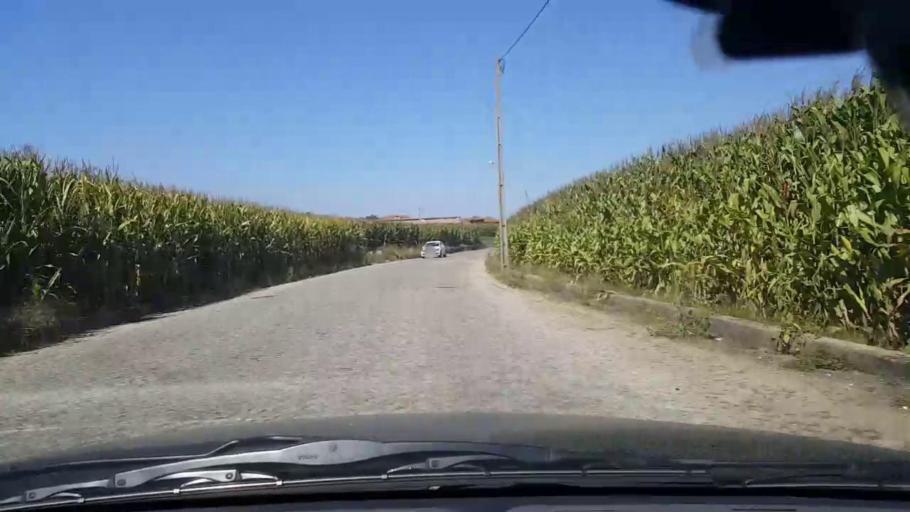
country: PT
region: Porto
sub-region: Matosinhos
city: Lavra
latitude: 41.2773
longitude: -8.7018
